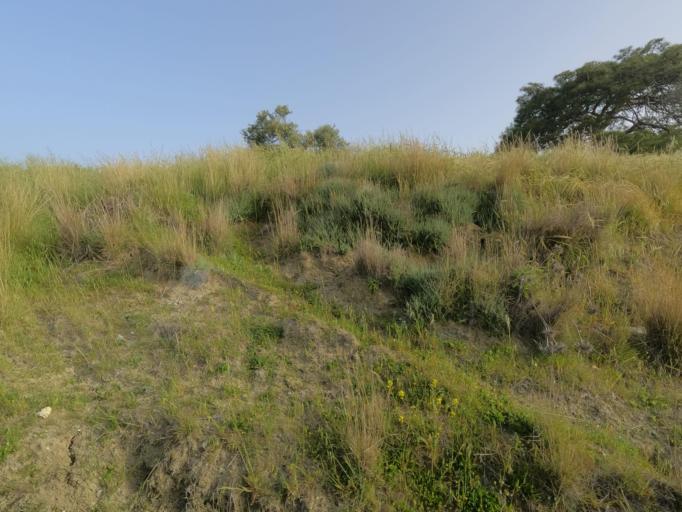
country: CY
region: Pafos
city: Polis
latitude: 34.9866
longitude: 32.3335
